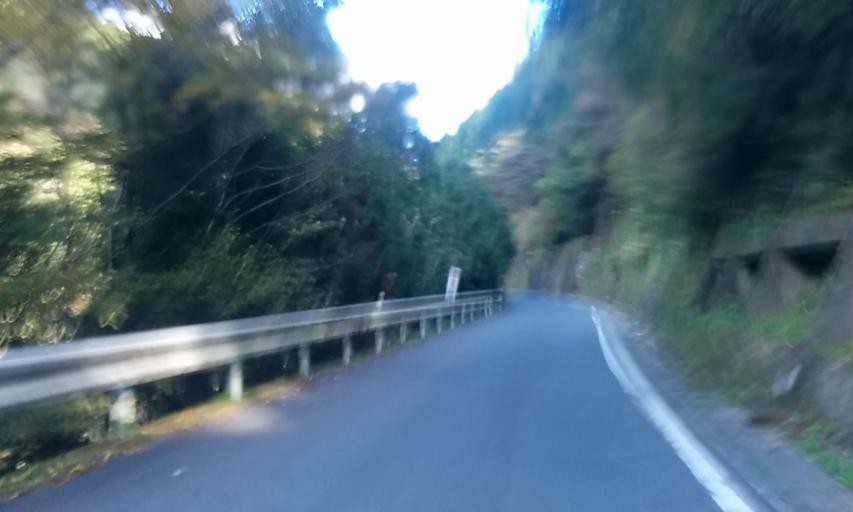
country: JP
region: Kyoto
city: Kameoka
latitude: 35.1288
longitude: 135.5704
